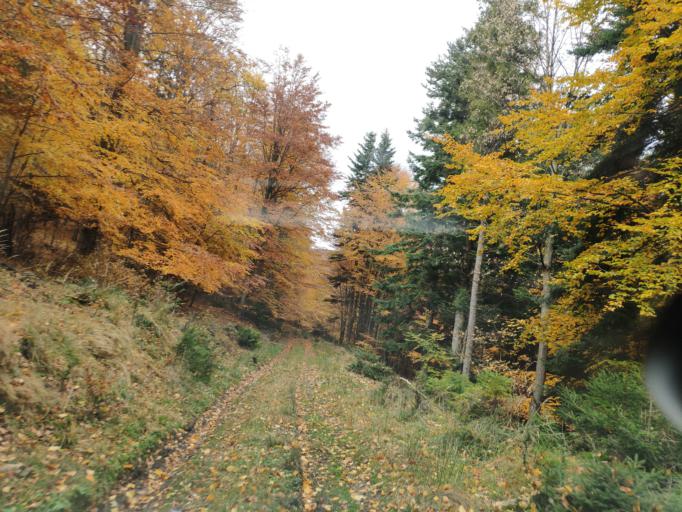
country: SK
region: Kosicky
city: Medzev
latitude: 48.7552
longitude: 20.9826
